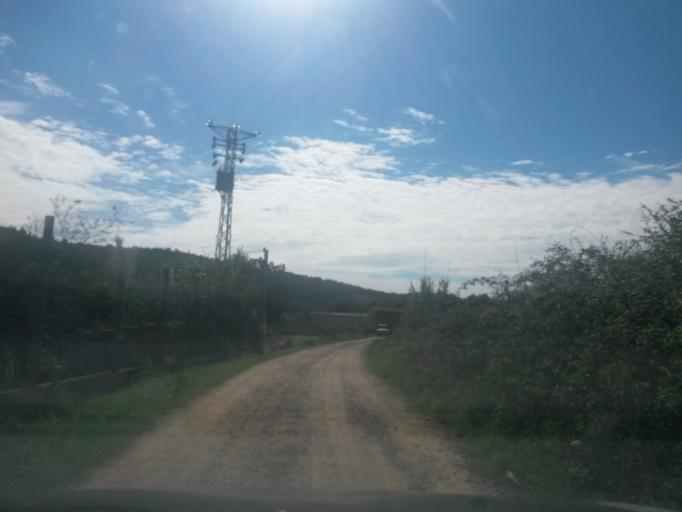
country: ES
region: Catalonia
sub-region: Provincia de Girona
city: la Cellera de Ter
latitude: 41.9858
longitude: 2.6215
